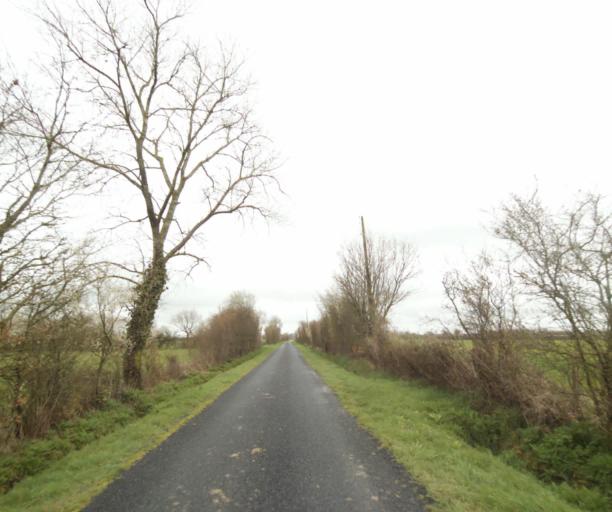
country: FR
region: Pays de la Loire
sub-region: Departement de la Loire-Atlantique
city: Bouvron
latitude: 47.4511
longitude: -1.8733
